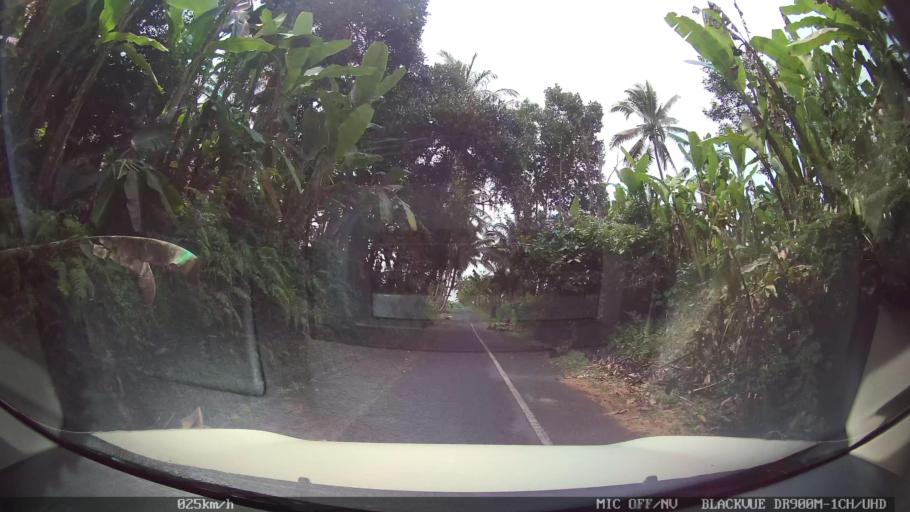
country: ID
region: Bali
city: Pemijian
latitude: -8.4410
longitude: 115.2263
